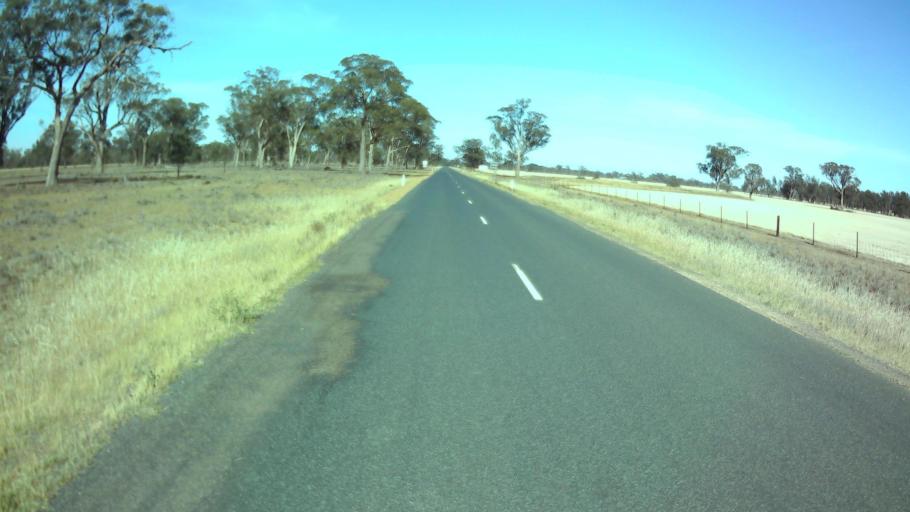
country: AU
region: New South Wales
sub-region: Weddin
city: Grenfell
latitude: -34.1368
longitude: 147.7623
